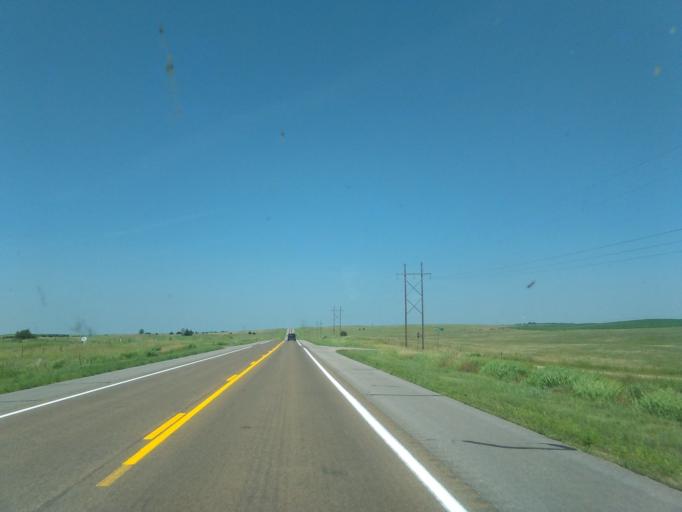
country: US
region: Nebraska
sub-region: Lincoln County
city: North Platte
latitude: 40.7711
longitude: -100.7402
